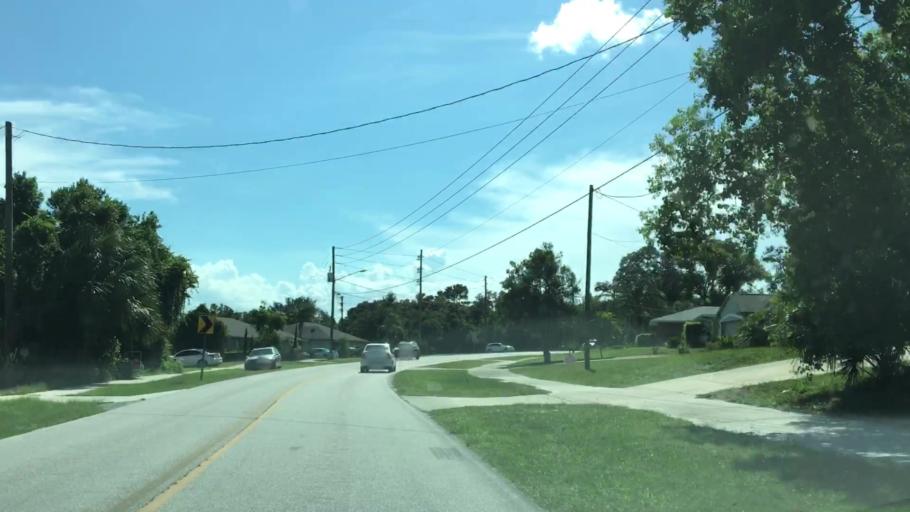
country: US
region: Florida
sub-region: Volusia County
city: Deltona
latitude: 28.9181
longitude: -81.2340
